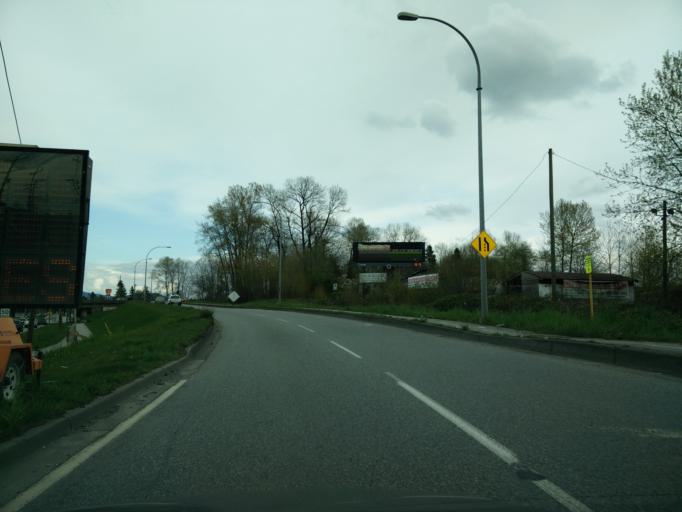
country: CA
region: British Columbia
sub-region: Fraser Valley Regional District
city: North Vancouver
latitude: 49.3046
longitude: -123.0300
